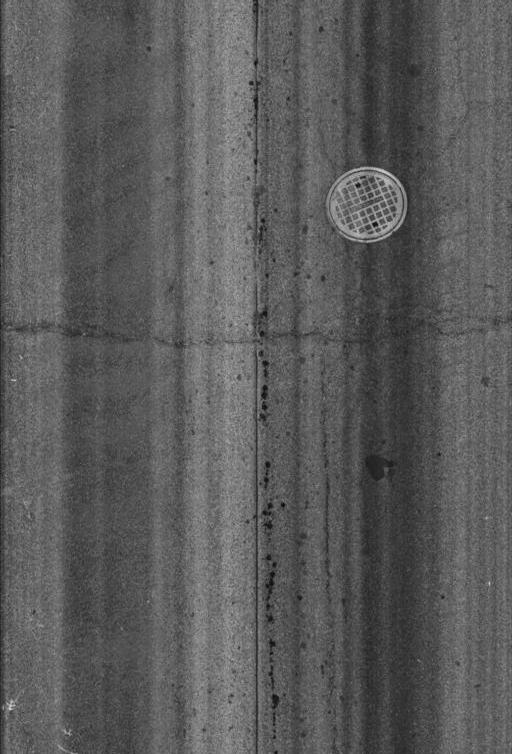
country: US
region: Maryland
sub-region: Prince George's County
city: Mount Rainier
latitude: 38.9242
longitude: -76.9742
